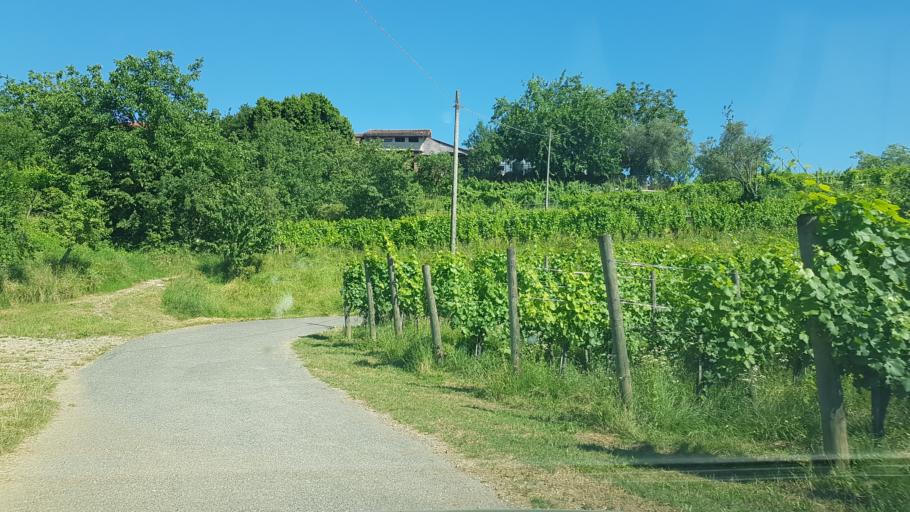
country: IT
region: Friuli Venezia Giulia
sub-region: Provincia di Gorizia
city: Capriva del Friuli
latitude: 45.9506
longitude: 13.5219
